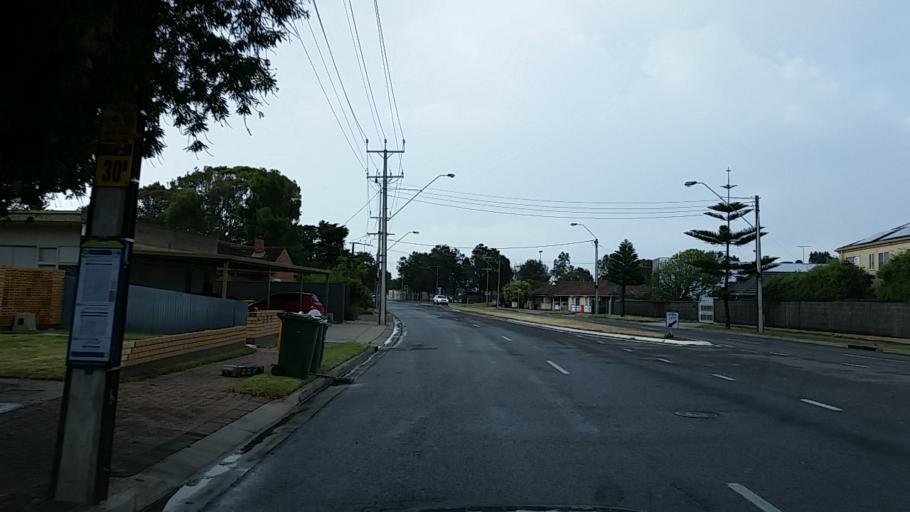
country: AU
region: South Australia
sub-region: Charles Sturt
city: Grange
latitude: -34.8988
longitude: 138.4902
